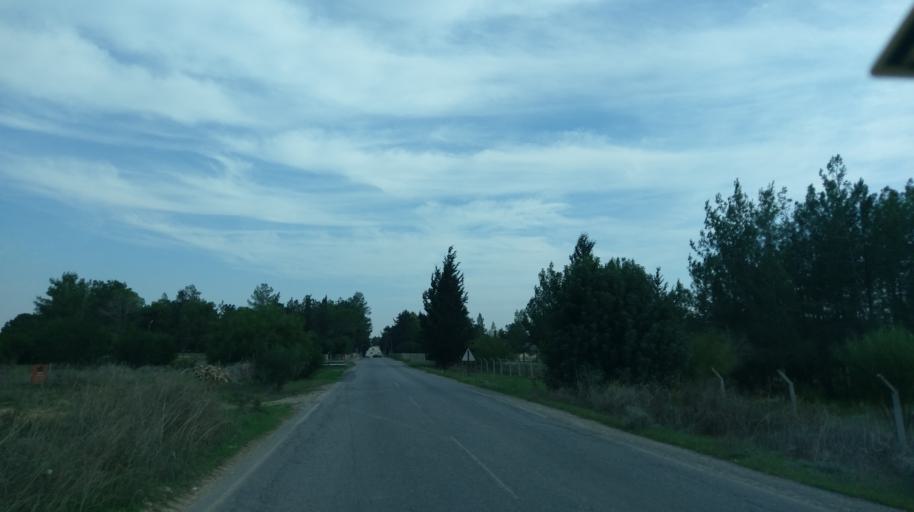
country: CY
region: Lefkosia
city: Mammari
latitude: 35.2356
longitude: 33.1609
